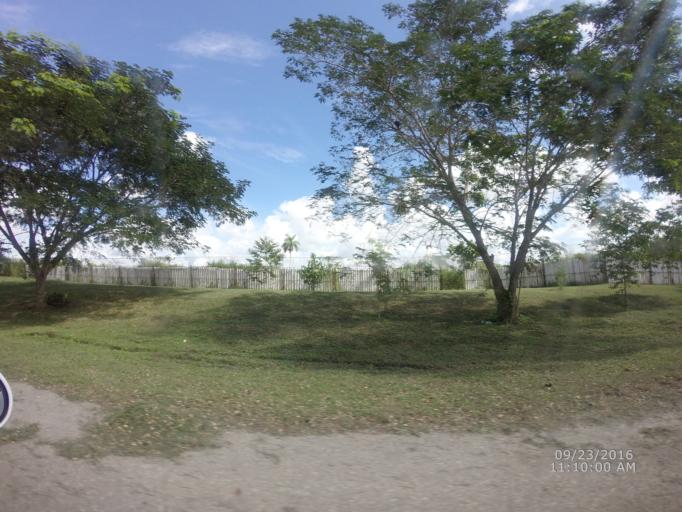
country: CU
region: La Habana
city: Arroyo Naranjo
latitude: 23.0194
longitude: -82.2524
